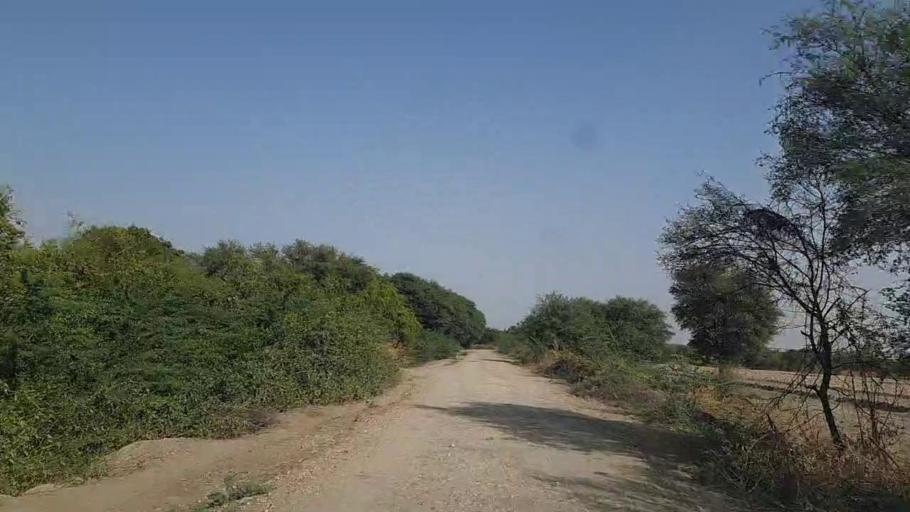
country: PK
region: Sindh
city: Naukot
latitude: 24.6096
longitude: 69.2829
